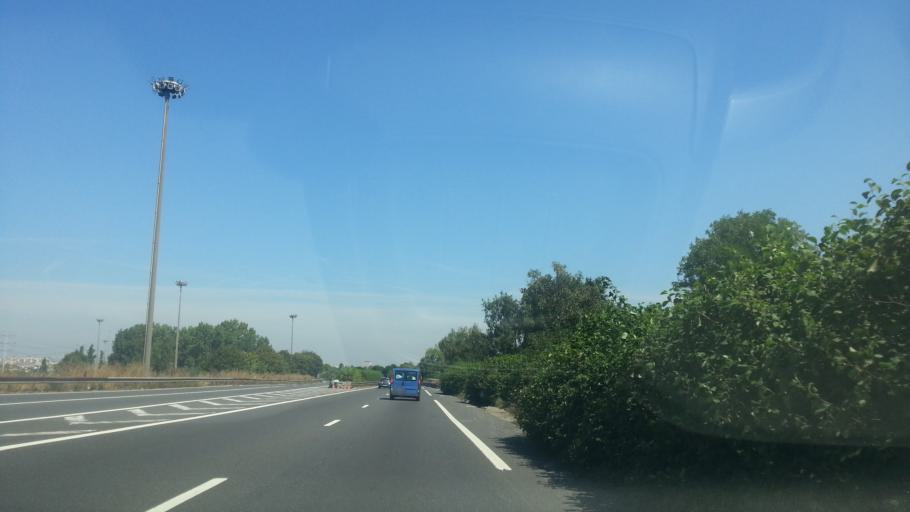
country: FR
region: Ile-de-France
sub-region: Departement de l'Essonne
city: Wissous
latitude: 48.7343
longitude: 2.3146
